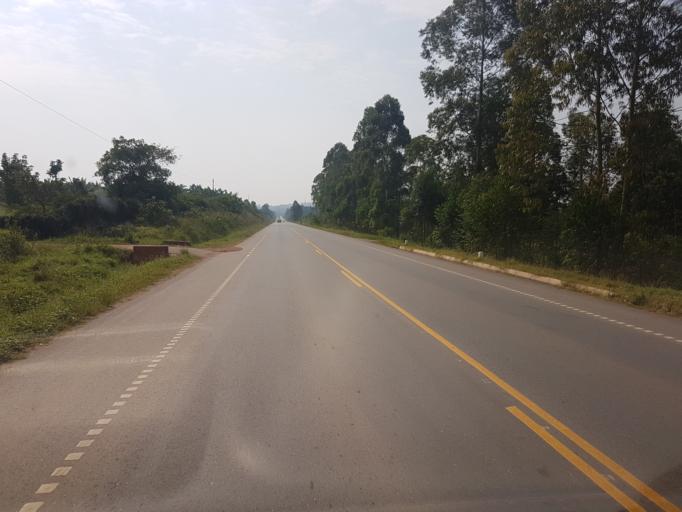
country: UG
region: Western Region
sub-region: Mbarara District
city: Bwizibwera
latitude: -0.6429
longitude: 30.5628
